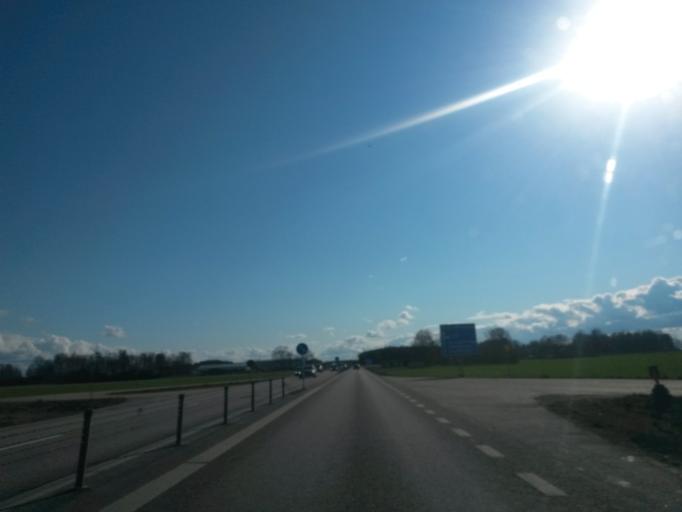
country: SE
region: Vaestra Goetaland
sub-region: Vara Kommun
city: Vara
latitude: 58.2832
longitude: 13.0248
